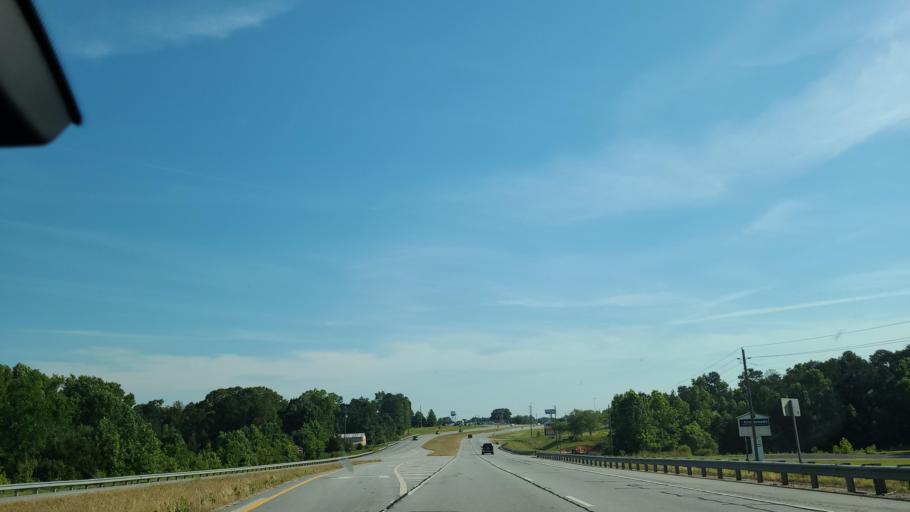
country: US
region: Georgia
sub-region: Jackson County
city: Commerce
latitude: 34.1777
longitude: -83.4432
